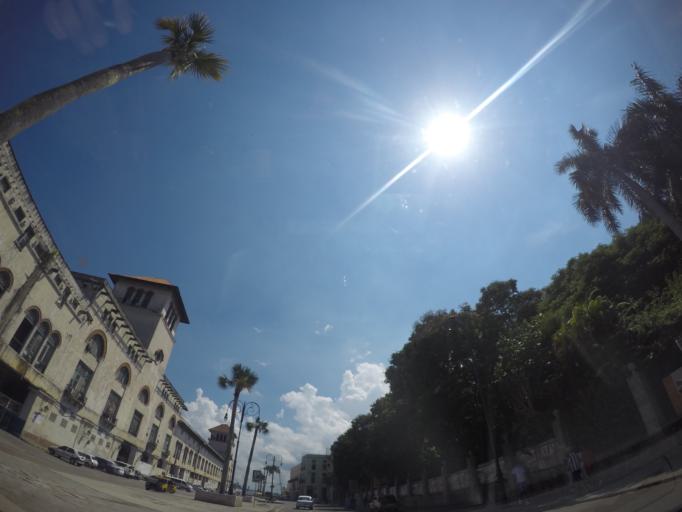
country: CU
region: La Habana
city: La Habana Vieja
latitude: 23.1369
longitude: -82.3480
